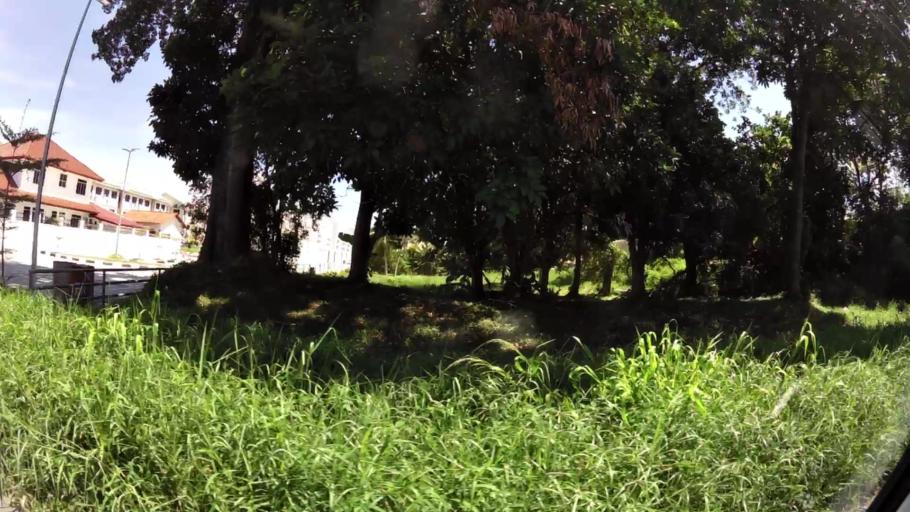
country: BN
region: Brunei and Muara
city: Bandar Seri Begawan
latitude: 4.9423
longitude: 114.9452
